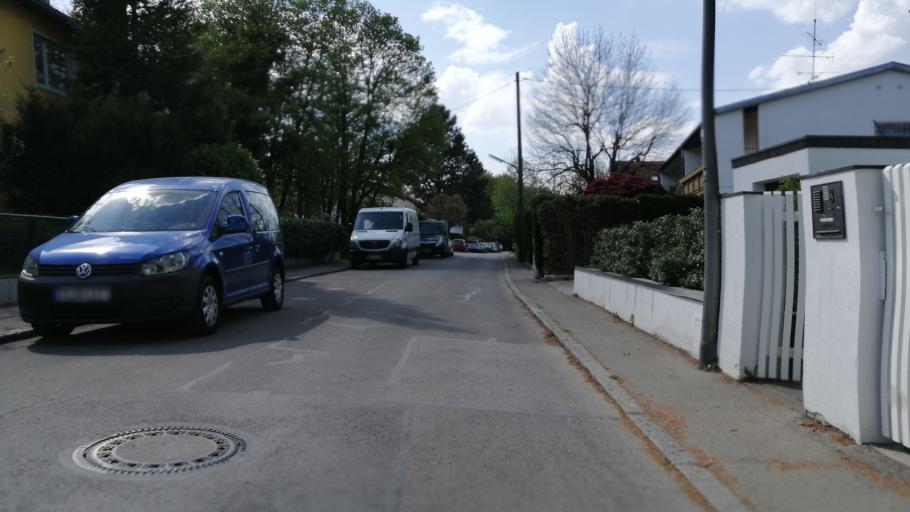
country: DE
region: Bavaria
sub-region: Upper Bavaria
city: Bogenhausen
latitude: 48.1498
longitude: 11.6375
